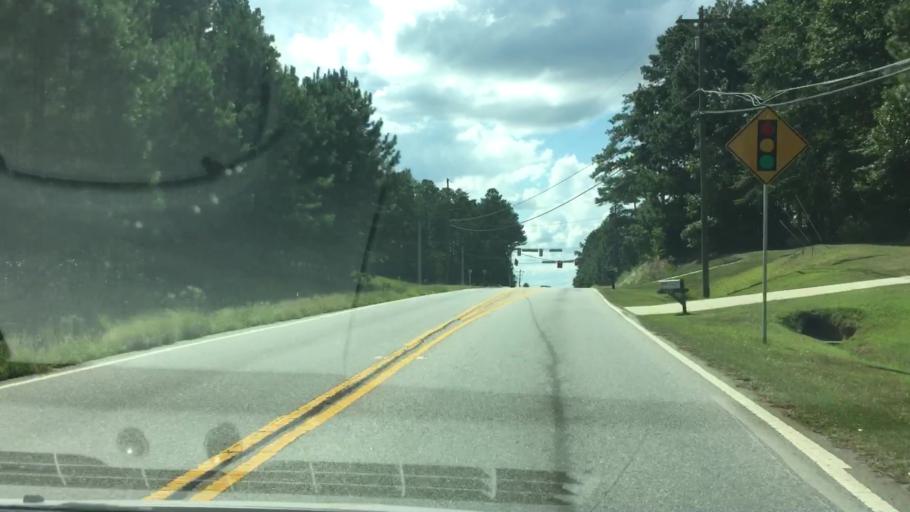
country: US
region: Georgia
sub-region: Fayette County
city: Fayetteville
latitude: 33.4573
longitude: -84.4066
